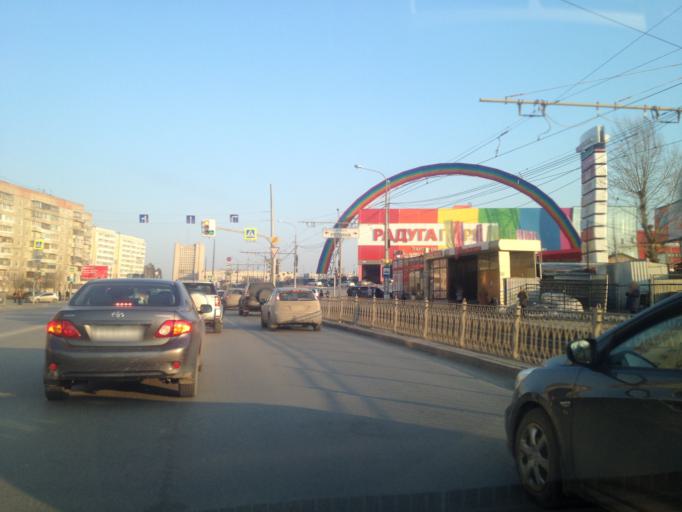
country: RU
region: Sverdlovsk
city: Shirokaya Rechka
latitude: 56.8196
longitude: 60.5371
